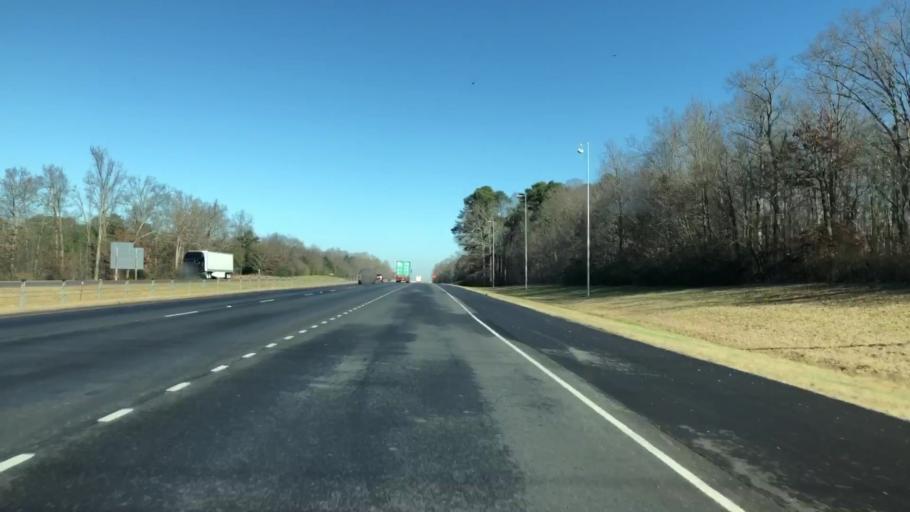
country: US
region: Alabama
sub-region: Limestone County
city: Athens
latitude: 34.7861
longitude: -86.9394
